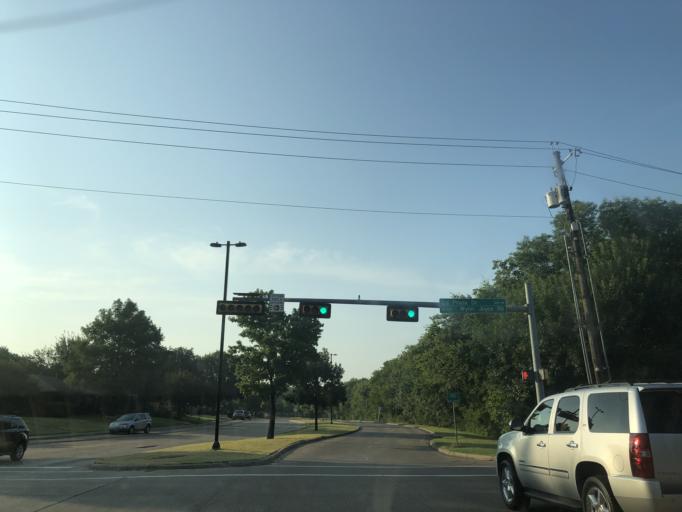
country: US
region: Texas
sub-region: Dallas County
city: Garland
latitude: 32.8565
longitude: -96.6161
